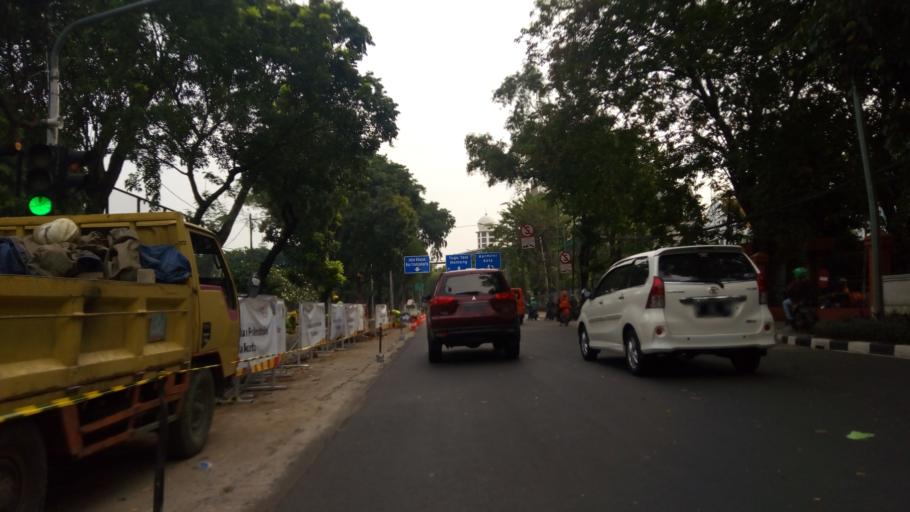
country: ID
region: Jakarta Raya
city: Jakarta
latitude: -6.1688
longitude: 106.8350
